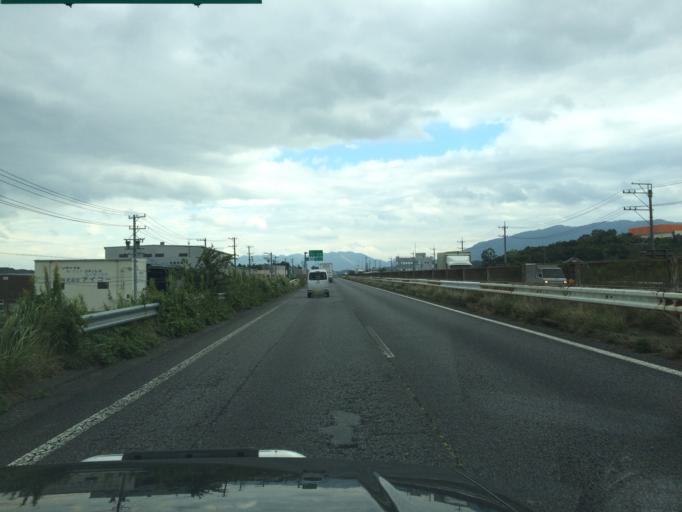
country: JP
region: Mie
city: Ueno-ebisumachi
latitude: 34.8017
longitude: 136.1852
